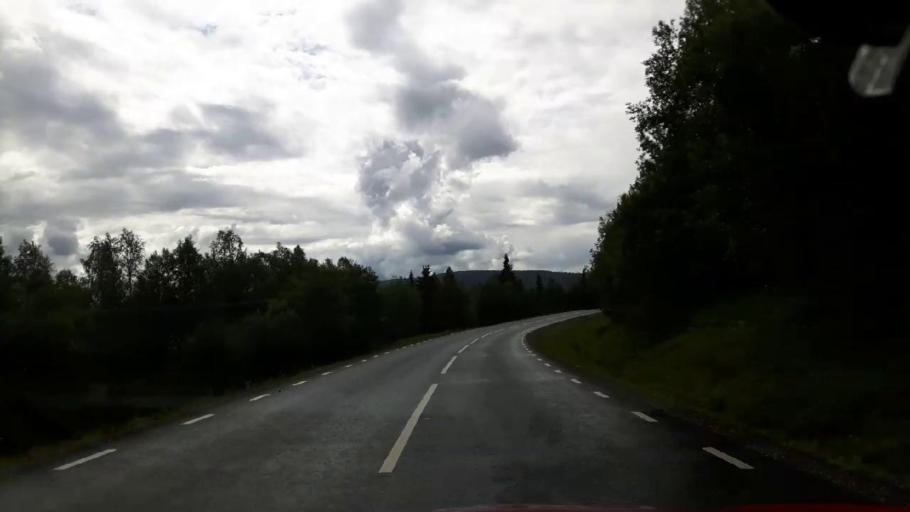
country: NO
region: Nord-Trondelag
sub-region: Royrvik
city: Royrvik
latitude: 64.8755
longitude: 14.2115
